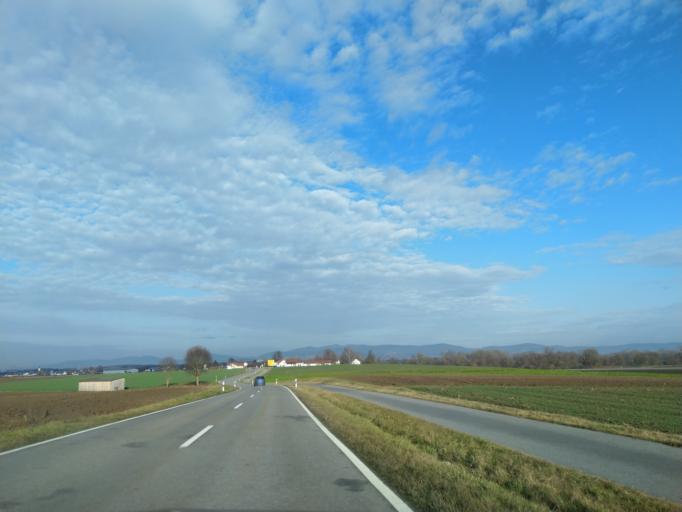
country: DE
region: Bavaria
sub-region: Lower Bavaria
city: Osterhofen
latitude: 48.7128
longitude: 13.0155
